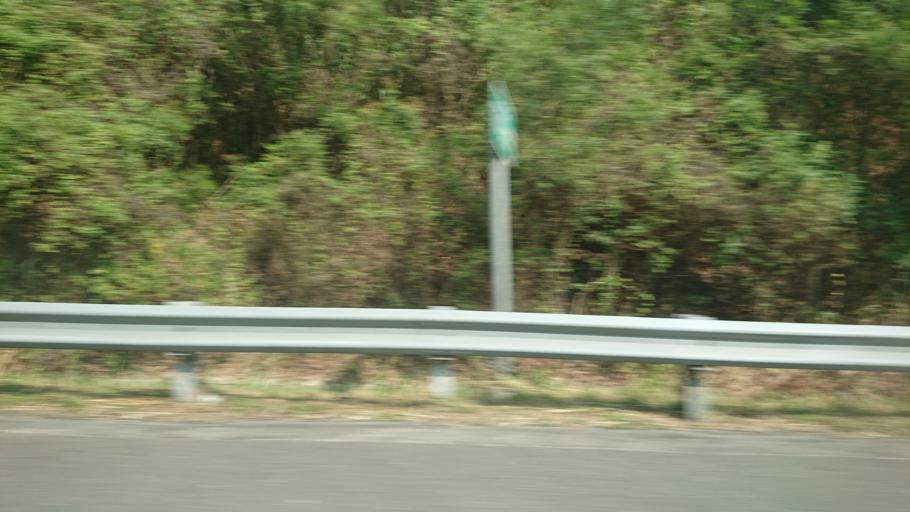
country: TW
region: Taiwan
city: Lugu
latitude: 23.7781
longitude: 120.6847
